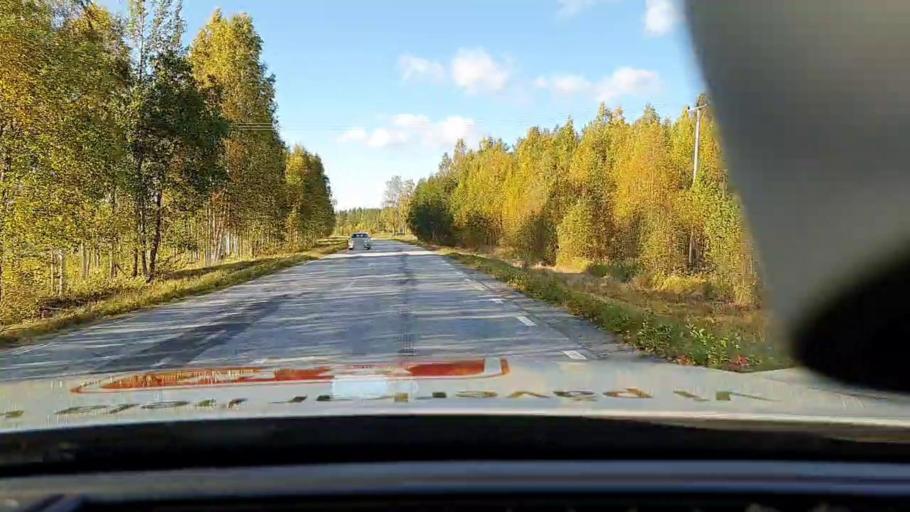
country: SE
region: Norrbotten
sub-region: Pitea Kommun
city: Norrfjarden
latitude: 65.4301
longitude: 21.4908
